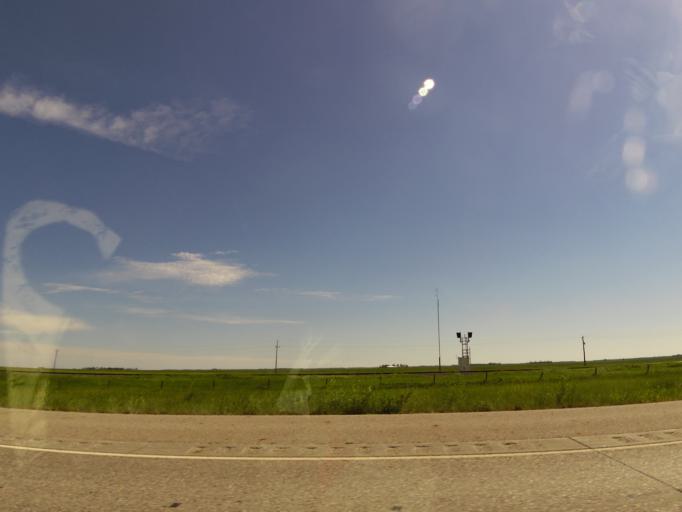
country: US
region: North Dakota
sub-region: Cass County
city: West Fargo
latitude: 47.0397
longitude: -96.9251
